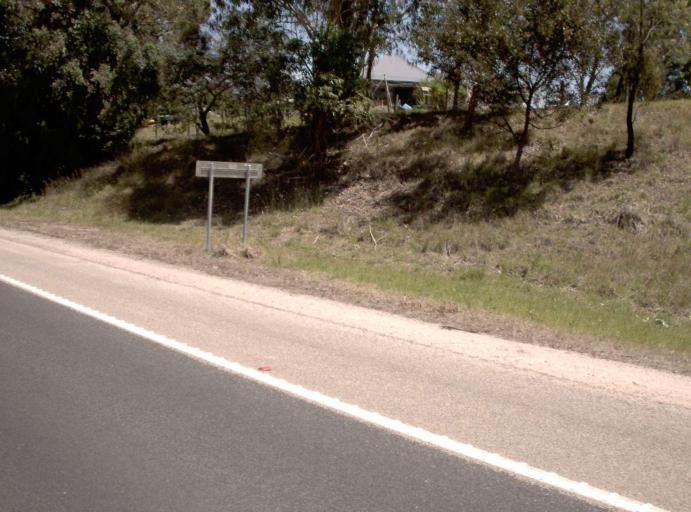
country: AU
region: Victoria
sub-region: East Gippsland
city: Bairnsdale
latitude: -37.7142
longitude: 147.8058
